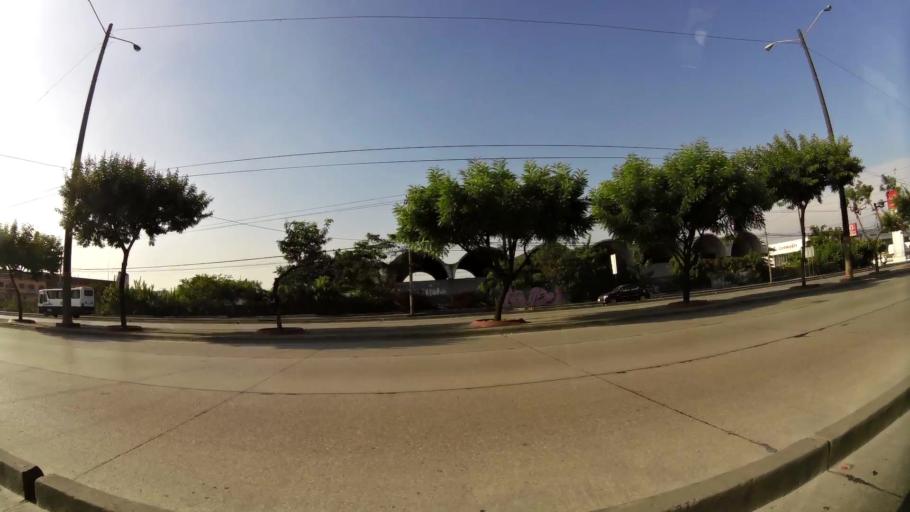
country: EC
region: Guayas
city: Guayaquil
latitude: -2.1464
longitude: -79.9134
